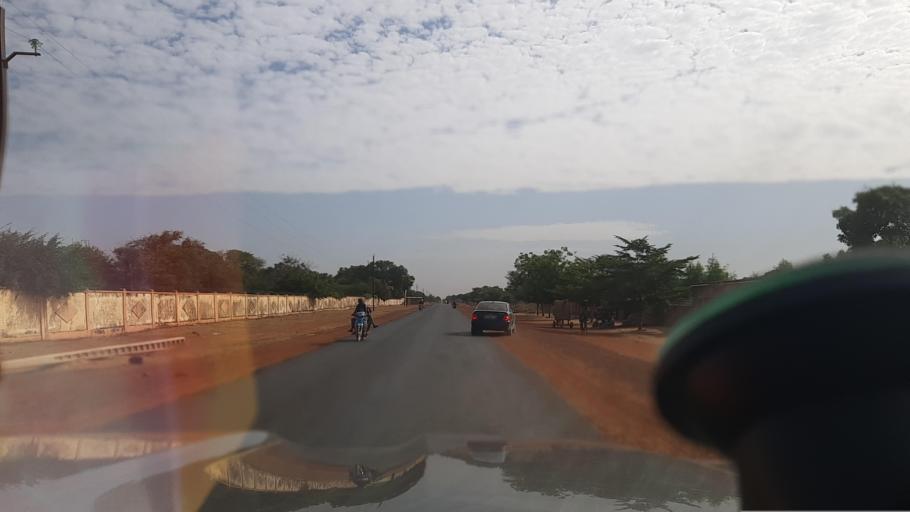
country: ML
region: Segou
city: Segou
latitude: 13.4969
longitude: -6.1643
